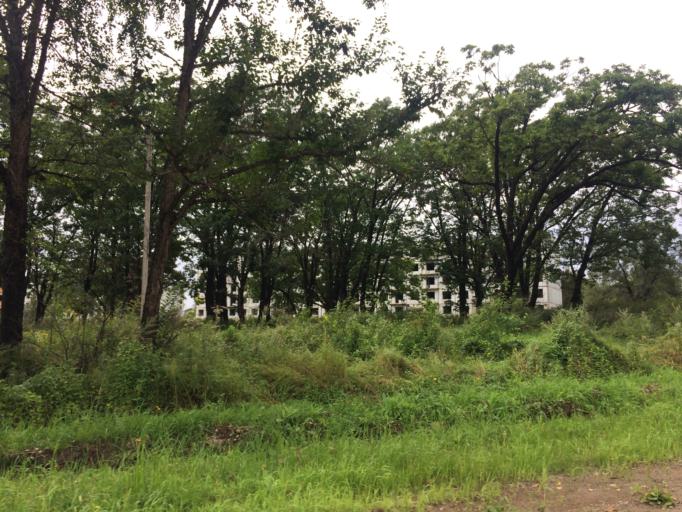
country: RU
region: Primorskiy
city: Lazo
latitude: 45.8236
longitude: 133.6438
